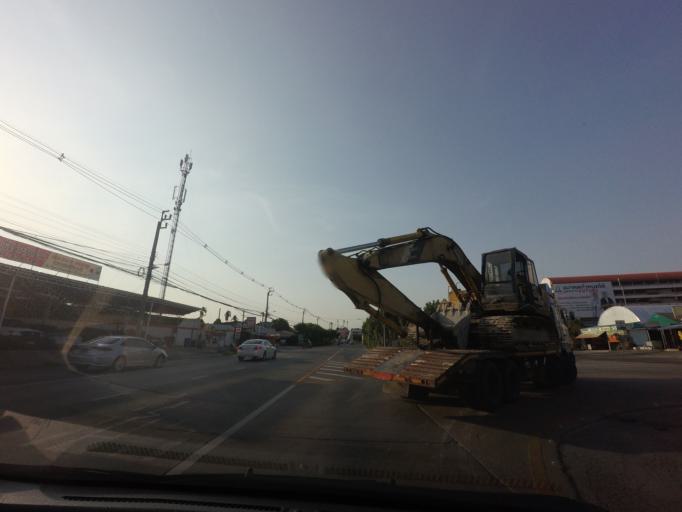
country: TH
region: Bangkok
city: Taling Chan
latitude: 13.7663
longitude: 100.4260
